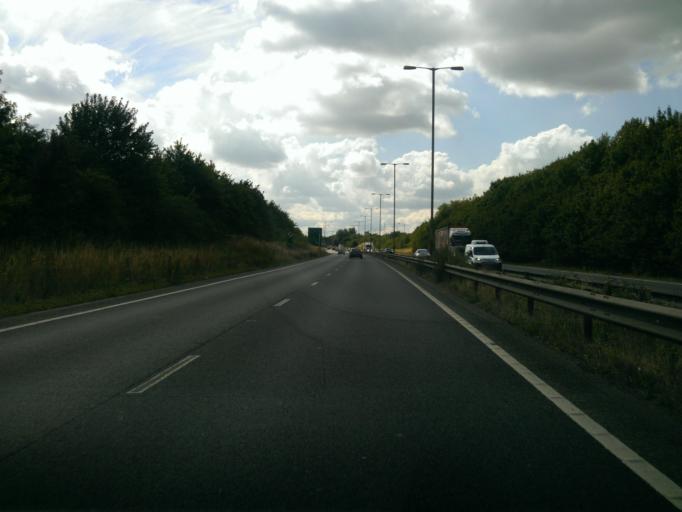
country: GB
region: England
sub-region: Northamptonshire
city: Rothwell
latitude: 52.4171
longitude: -0.8049
